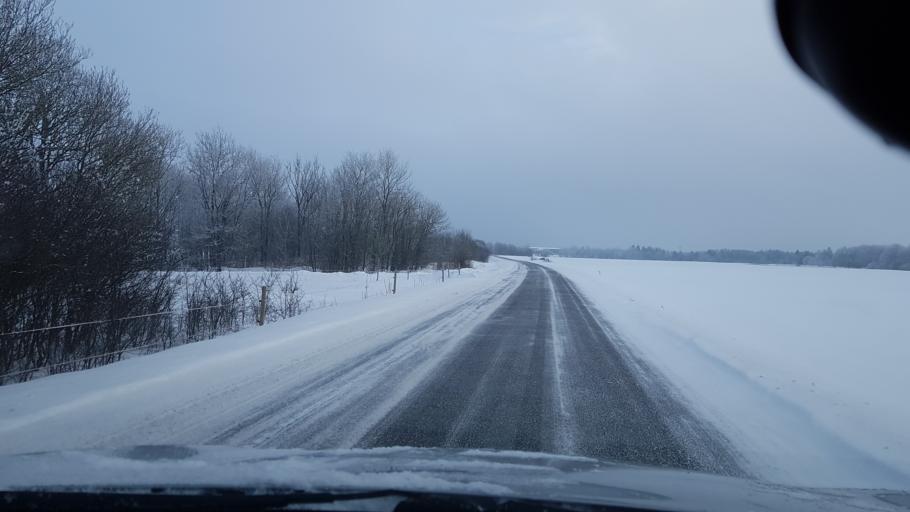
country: EE
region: Harju
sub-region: Keila linn
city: Keila
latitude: 59.3355
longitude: 24.4582
